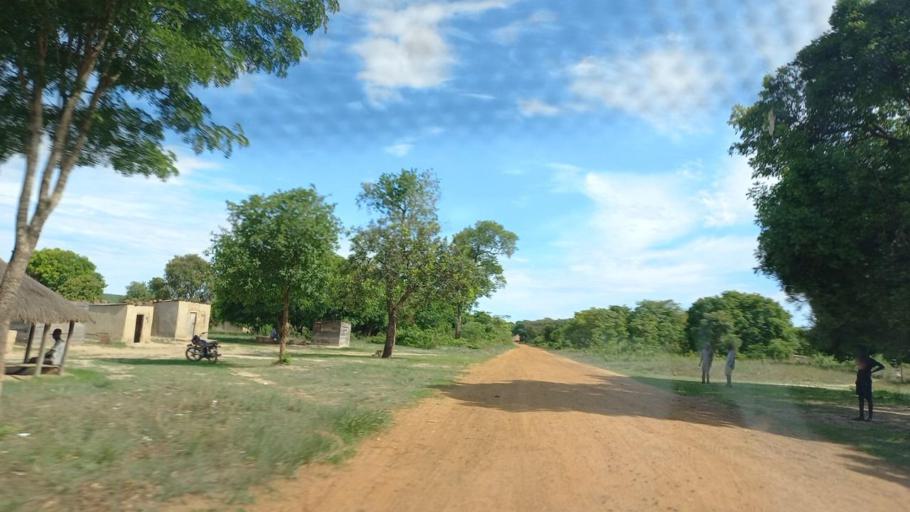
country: ZM
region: North-Western
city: Kabompo
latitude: -13.0603
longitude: 24.2193
